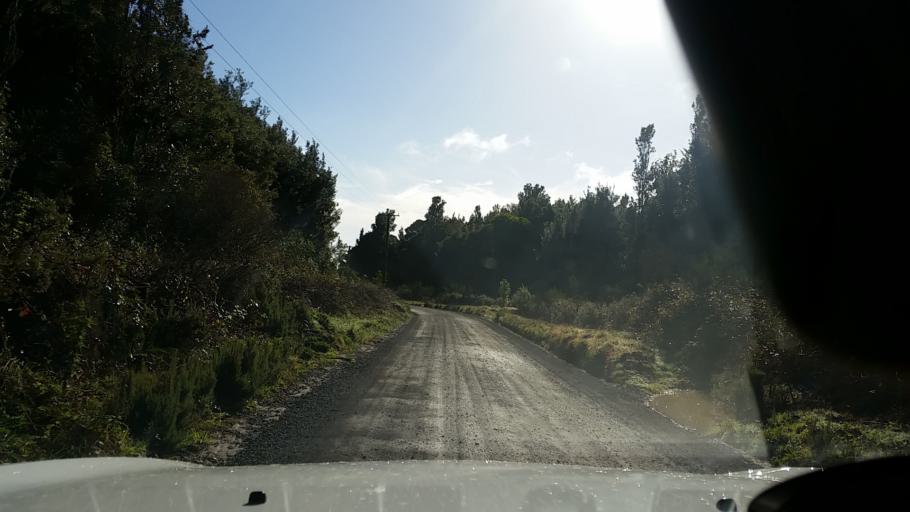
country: NZ
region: Bay of Plenty
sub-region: Kawerau District
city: Kawerau
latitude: -38.0142
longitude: 176.4899
